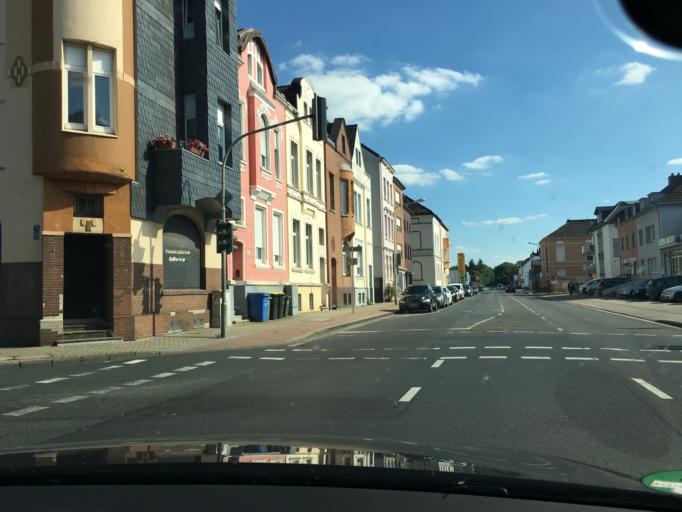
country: DE
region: North Rhine-Westphalia
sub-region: Regierungsbezirk Koln
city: Dueren
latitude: 50.7905
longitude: 6.4897
